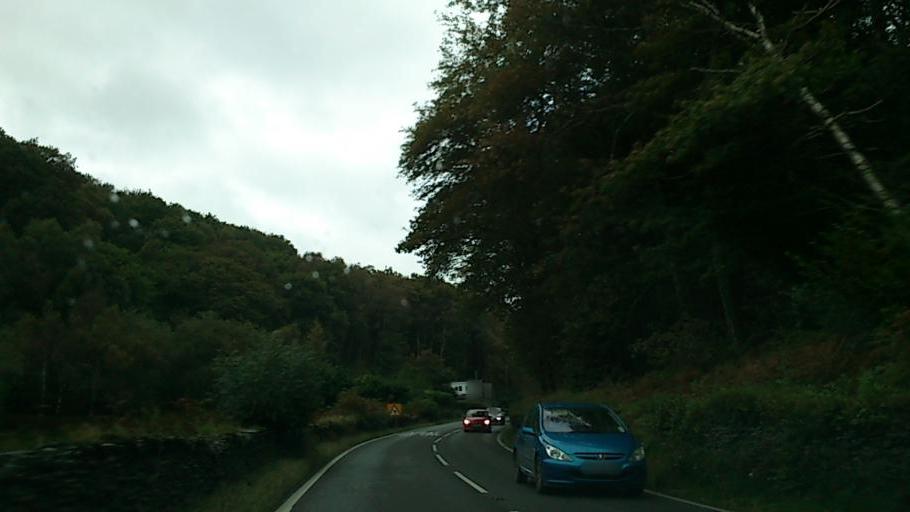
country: GB
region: Wales
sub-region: County of Ceredigion
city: Bow Street
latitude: 52.5174
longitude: -3.9722
